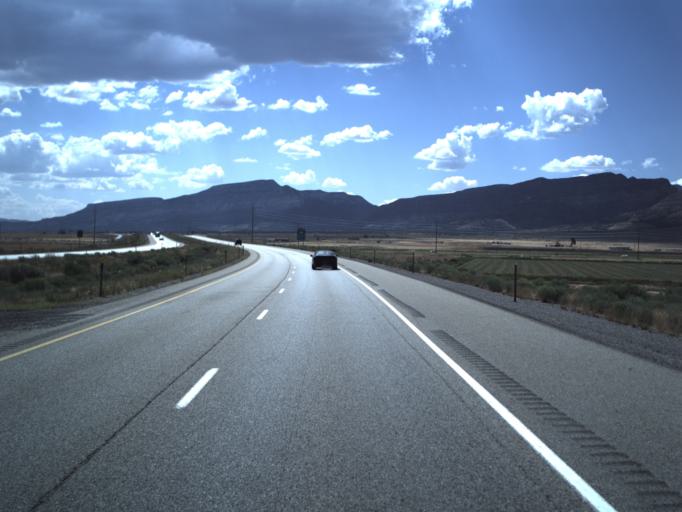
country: US
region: Utah
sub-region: Sevier County
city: Aurora
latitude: 38.8795
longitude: -111.9491
